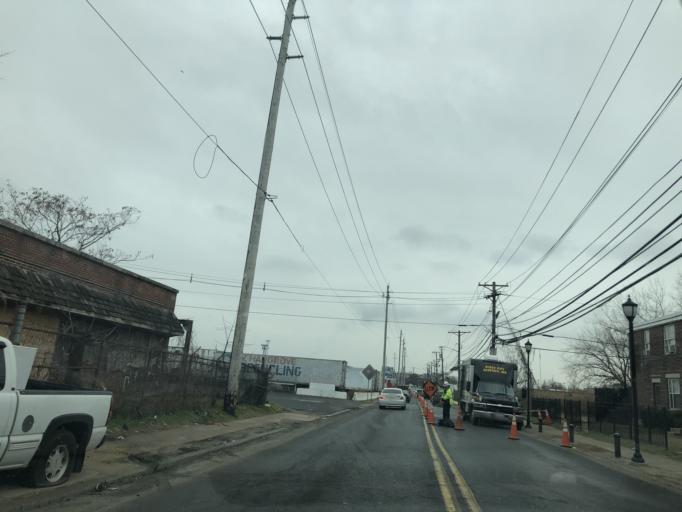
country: US
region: New Jersey
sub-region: Camden County
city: Camden
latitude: 39.9480
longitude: -75.1015
